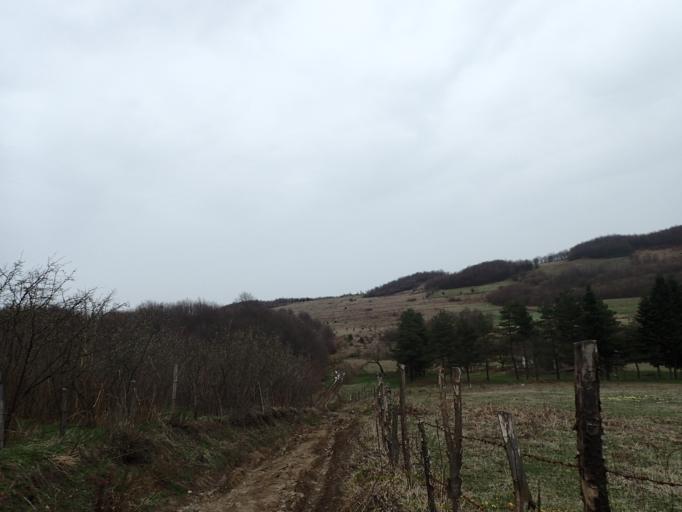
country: TR
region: Ordu
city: Kumru
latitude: 40.8119
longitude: 37.1636
